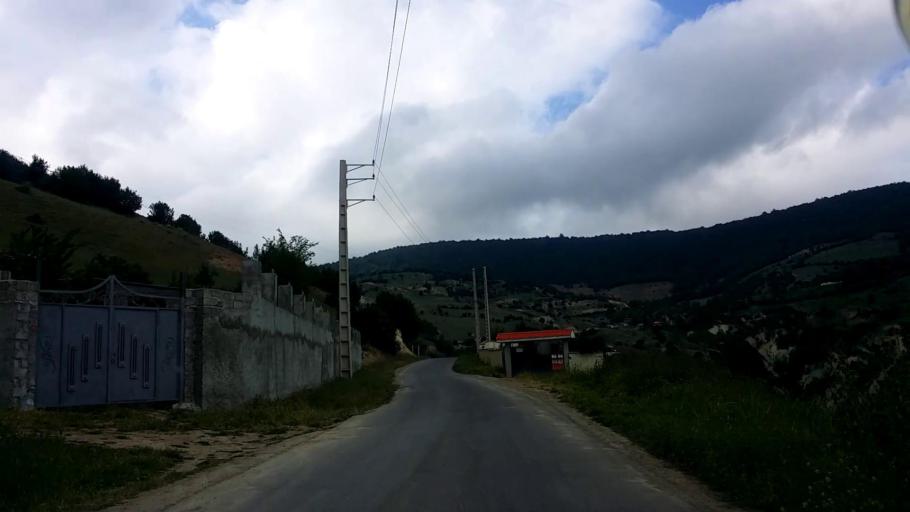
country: IR
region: Mazandaran
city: Chalus
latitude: 36.5499
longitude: 51.2700
